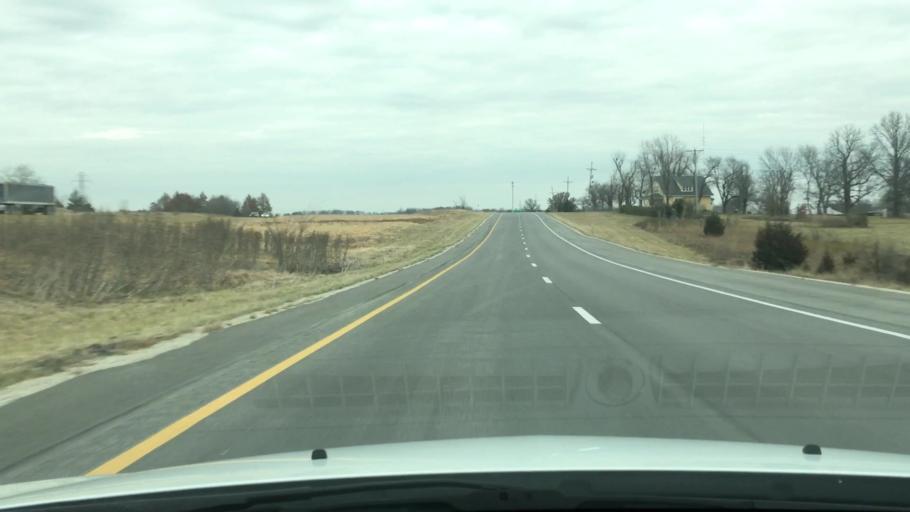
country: US
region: Missouri
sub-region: Audrain County
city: Mexico
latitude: 39.0970
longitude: -91.8982
